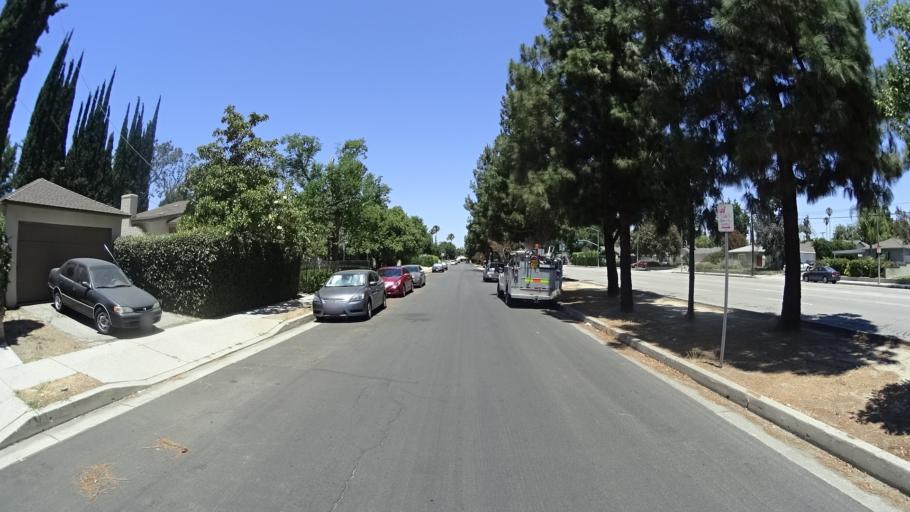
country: US
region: California
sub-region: Los Angeles County
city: Northridge
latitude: 34.1967
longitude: -118.5014
